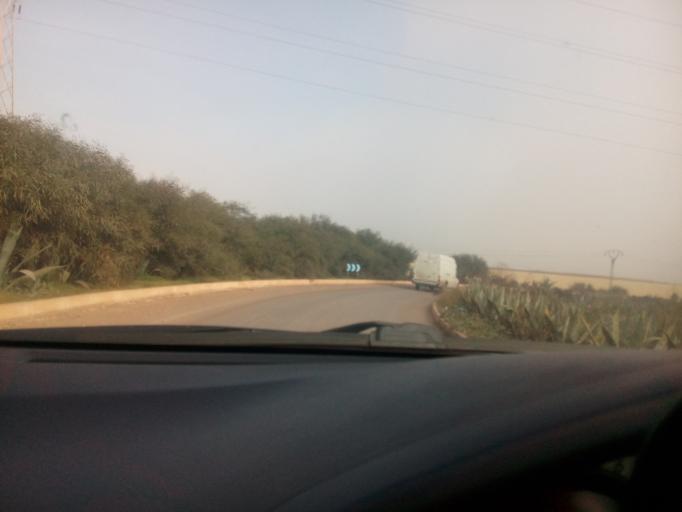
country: DZ
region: Oran
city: Es Senia
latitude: 35.6582
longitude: -0.6179
